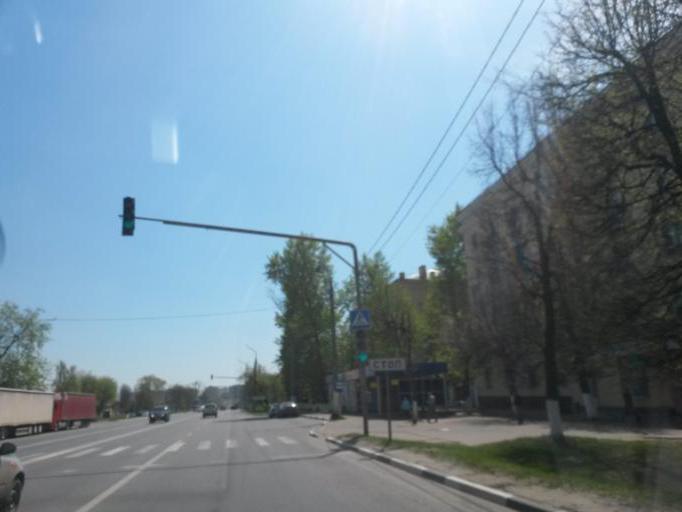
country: RU
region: Moskovskaya
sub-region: Podol'skiy Rayon
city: Podol'sk
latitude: 55.4159
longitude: 37.5478
